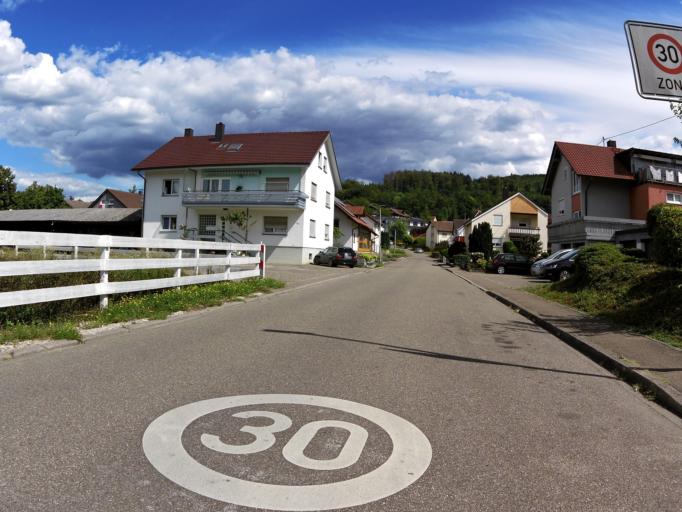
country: DE
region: Baden-Wuerttemberg
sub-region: Freiburg Region
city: Lahr
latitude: 48.3154
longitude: 7.8611
